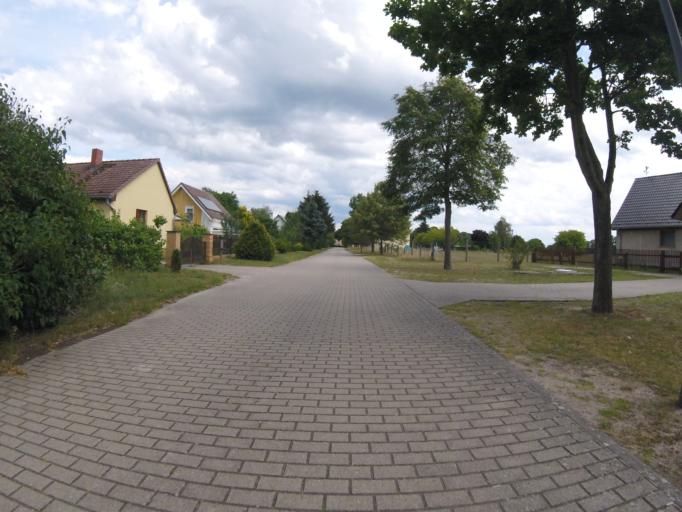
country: DE
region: Brandenburg
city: Gross Koris
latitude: 52.1504
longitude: 13.6779
